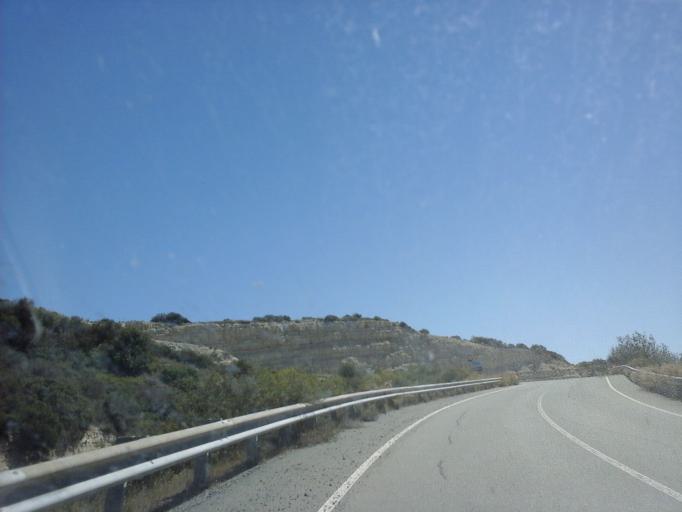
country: CY
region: Limassol
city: Pissouri
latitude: 34.6685
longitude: 32.6617
